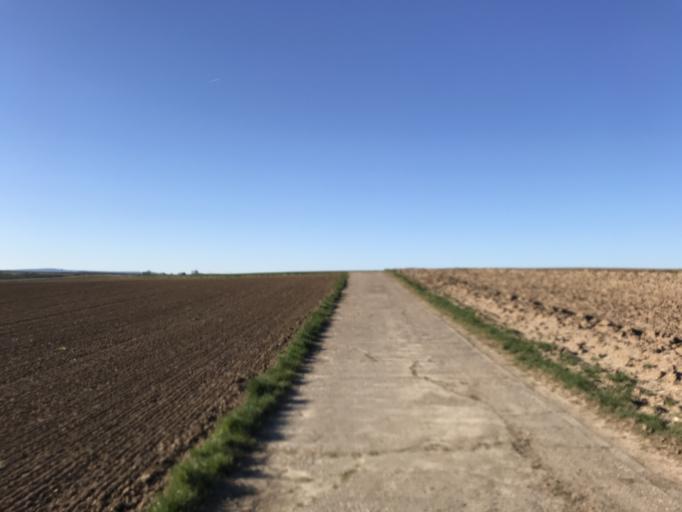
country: DE
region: Rheinland-Pfalz
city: Klein-Winternheim
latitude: 49.9362
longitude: 8.2317
